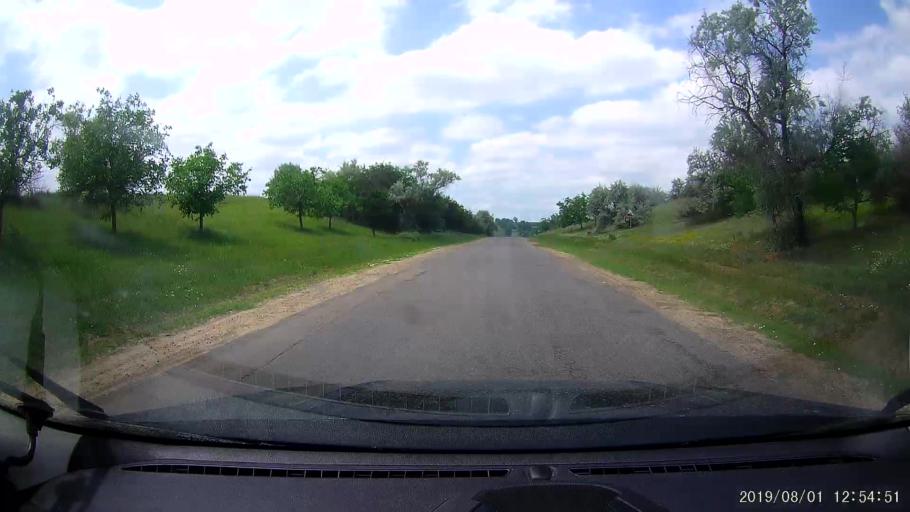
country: MD
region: Gagauzia
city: Vulcanesti
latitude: 45.6946
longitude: 28.4790
